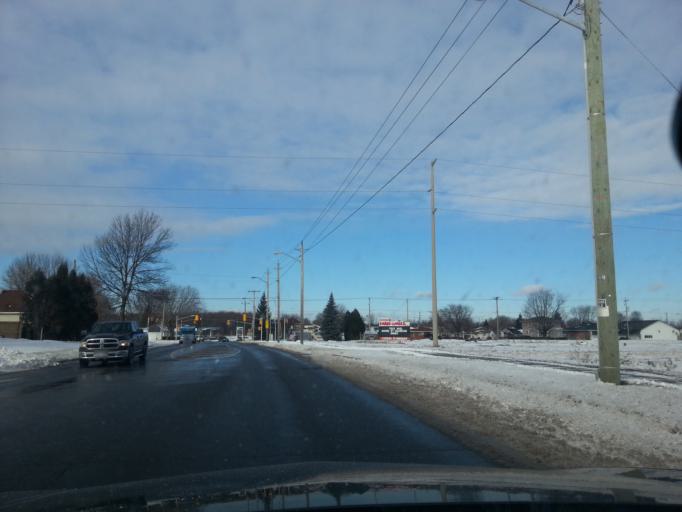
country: CA
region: Ontario
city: Cornwall
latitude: 45.0332
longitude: -74.7221
